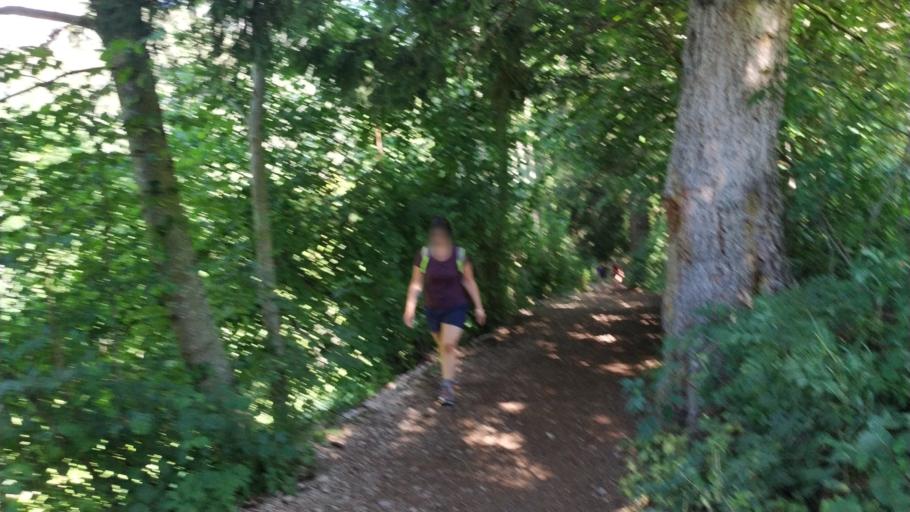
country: IT
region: Trentino-Alto Adige
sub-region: Bolzano
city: San Felice
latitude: 46.4792
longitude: 11.1324
